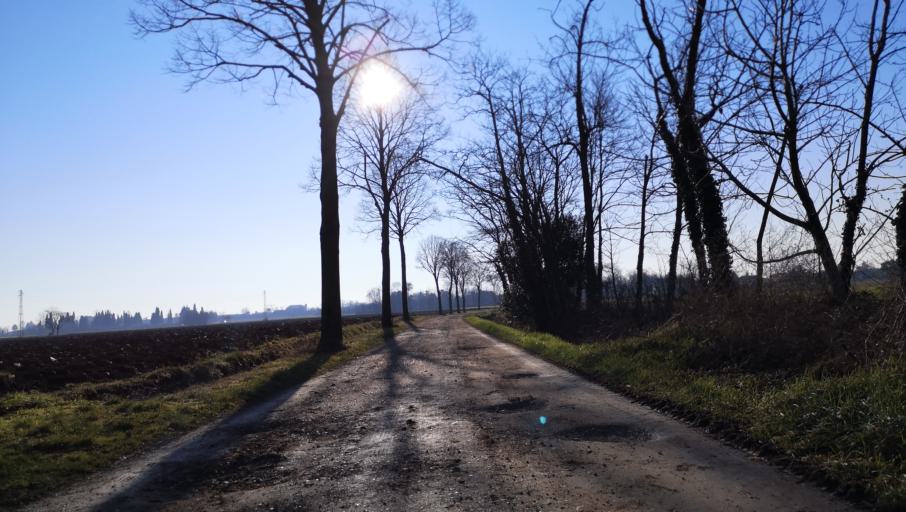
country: IT
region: Friuli Venezia Giulia
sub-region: Provincia di Udine
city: Palmanova
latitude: 45.9178
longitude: 13.2984
